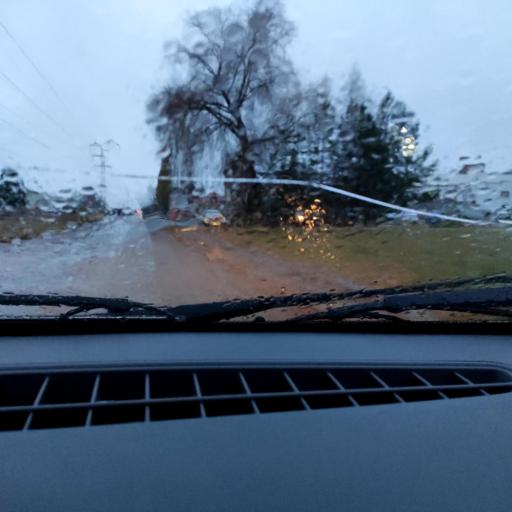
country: RU
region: Bashkortostan
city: Avdon
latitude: 54.6859
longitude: 55.8052
